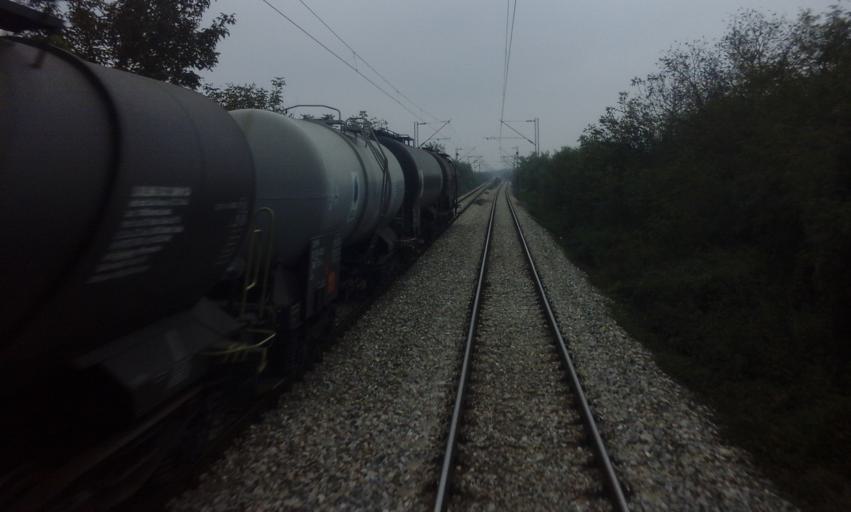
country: RS
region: Central Serbia
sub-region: Sumadijski Okrug
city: Lapovo
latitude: 44.2264
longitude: 21.0955
